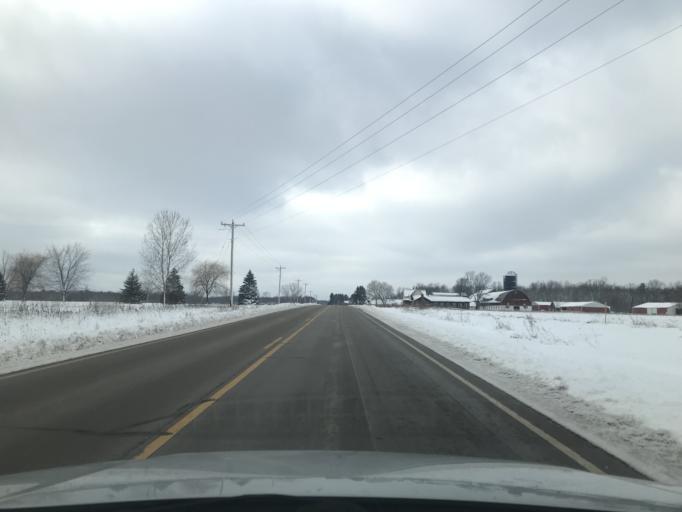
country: US
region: Wisconsin
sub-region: Oconto County
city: Oconto
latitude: 44.9502
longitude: -87.9611
